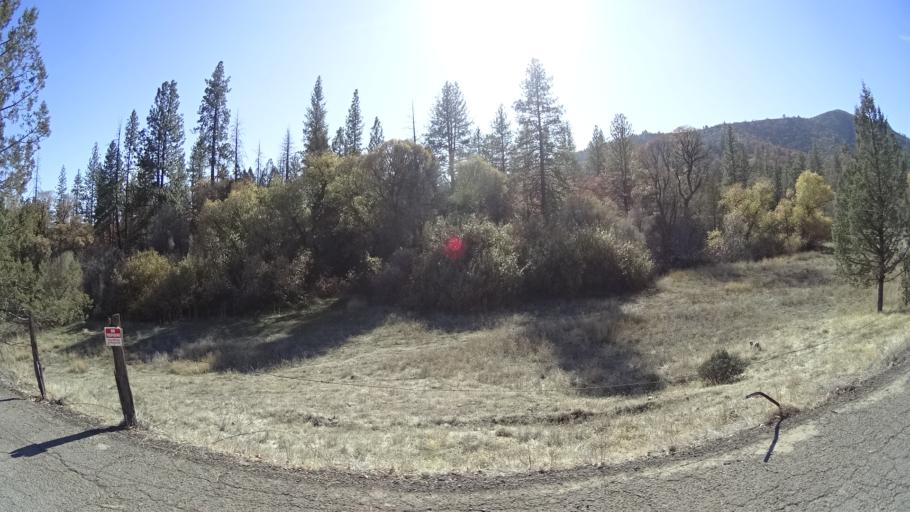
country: US
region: California
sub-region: Siskiyou County
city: Yreka
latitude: 41.7607
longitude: -122.6342
